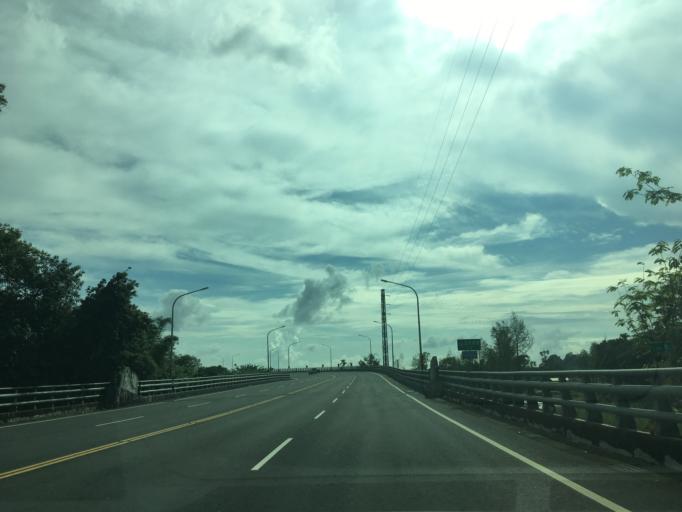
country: TW
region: Taiwan
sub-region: Chiayi
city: Jiayi Shi
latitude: 23.4530
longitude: 120.5540
